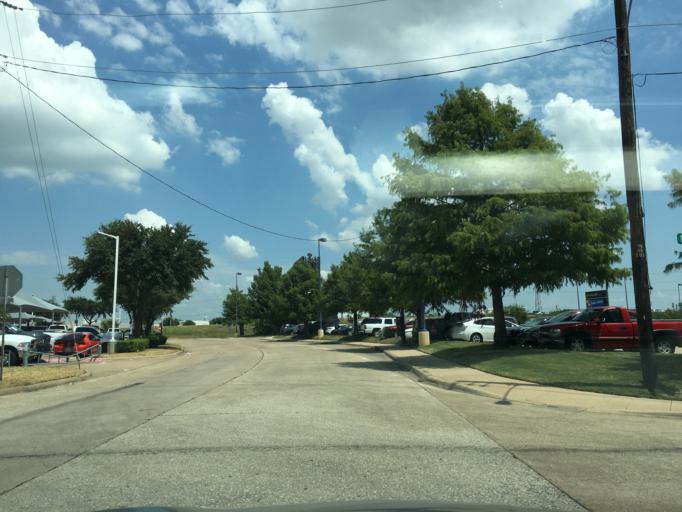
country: US
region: Texas
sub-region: Dallas County
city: Garland
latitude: 32.8696
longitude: -96.6776
